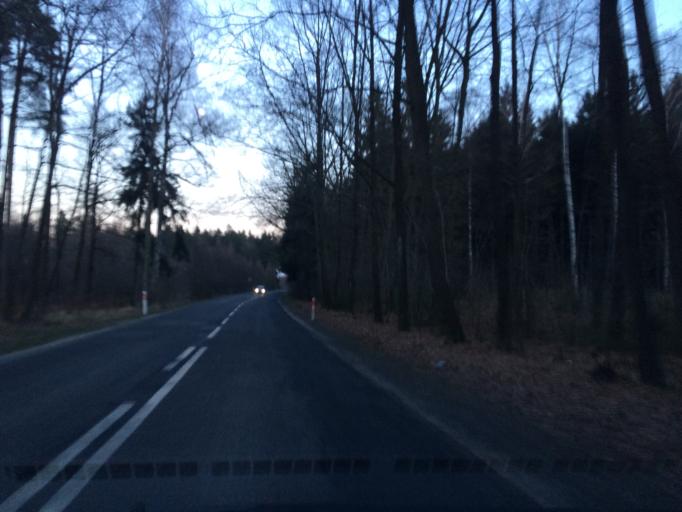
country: PL
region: Lower Silesian Voivodeship
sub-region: Powiat zlotoryjski
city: Olszanica
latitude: 51.1184
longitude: 15.7560
